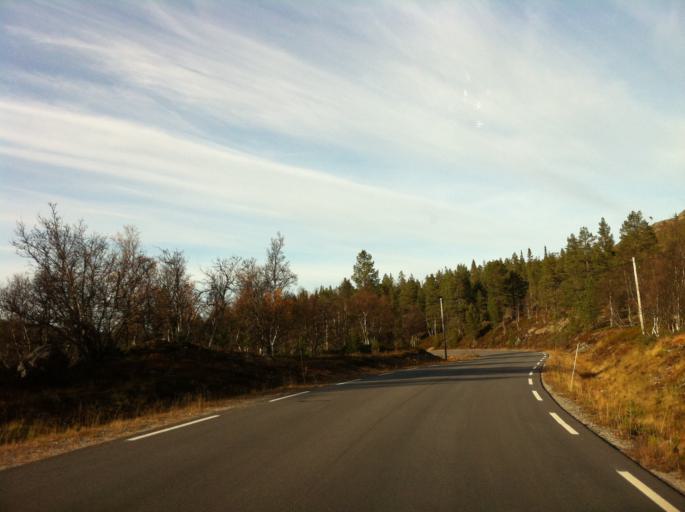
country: NO
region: Hedmark
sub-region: Engerdal
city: Engerdal
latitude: 62.0897
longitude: 12.0502
